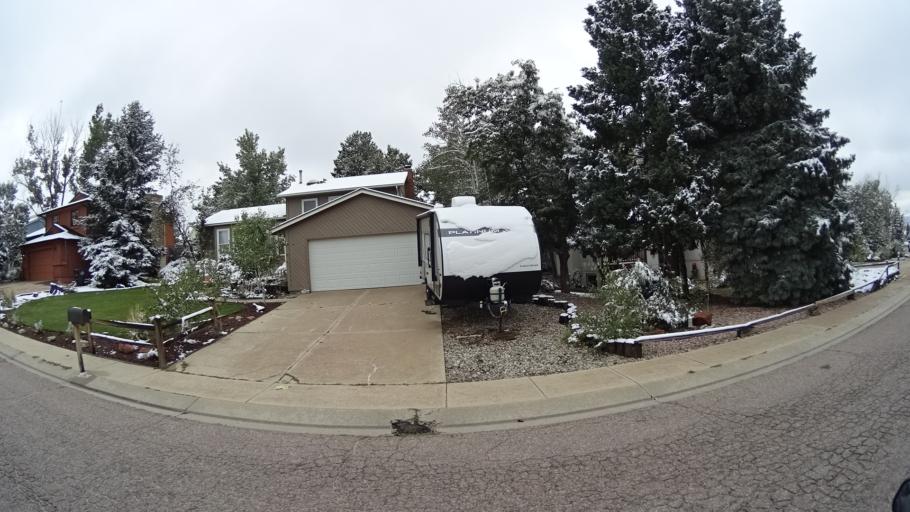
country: US
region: Colorado
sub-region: El Paso County
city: Cimarron Hills
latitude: 38.9218
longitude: -104.7722
